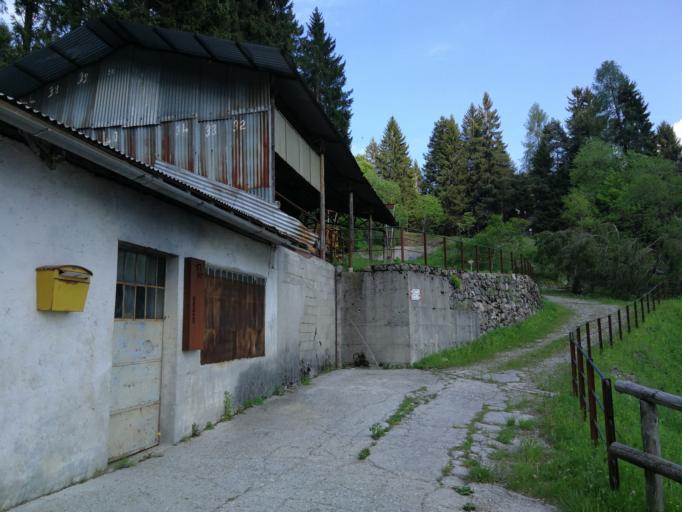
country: IT
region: Trentino-Alto Adige
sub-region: Provincia di Trento
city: Lodrone-Darzo
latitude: 45.8540
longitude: 10.5410
